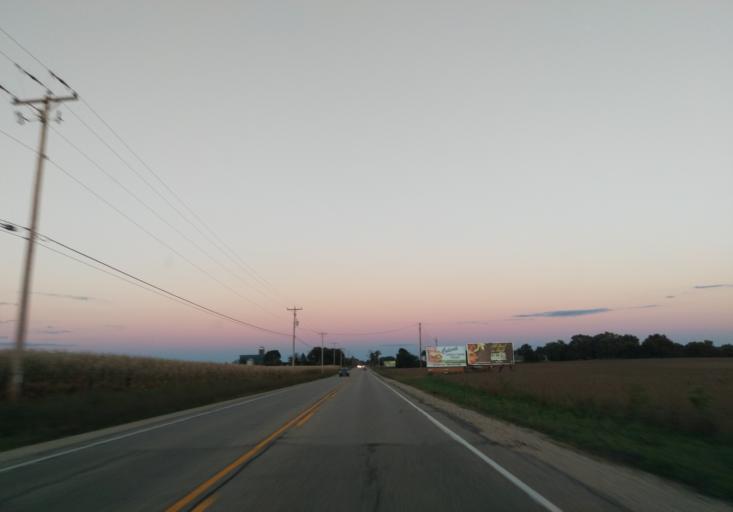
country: US
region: Wisconsin
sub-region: Rock County
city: Janesville
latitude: 42.7304
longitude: -89.1114
